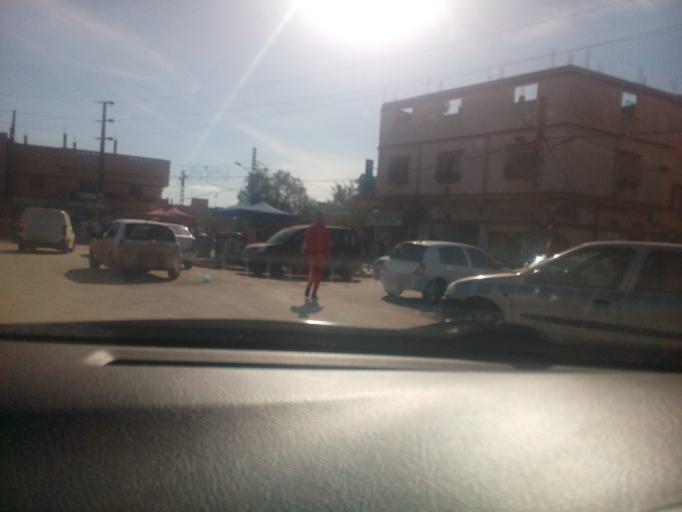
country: DZ
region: Oran
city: Sidi ech Chahmi
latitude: 35.6526
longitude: -0.5682
